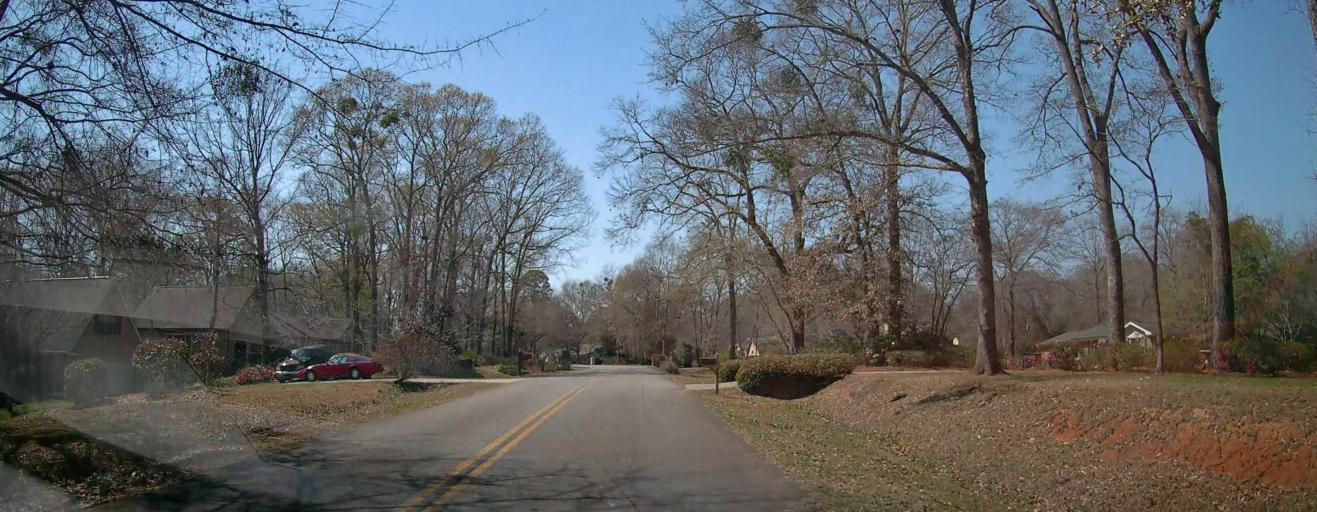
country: US
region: Georgia
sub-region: Houston County
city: Centerville
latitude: 32.5912
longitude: -83.6971
